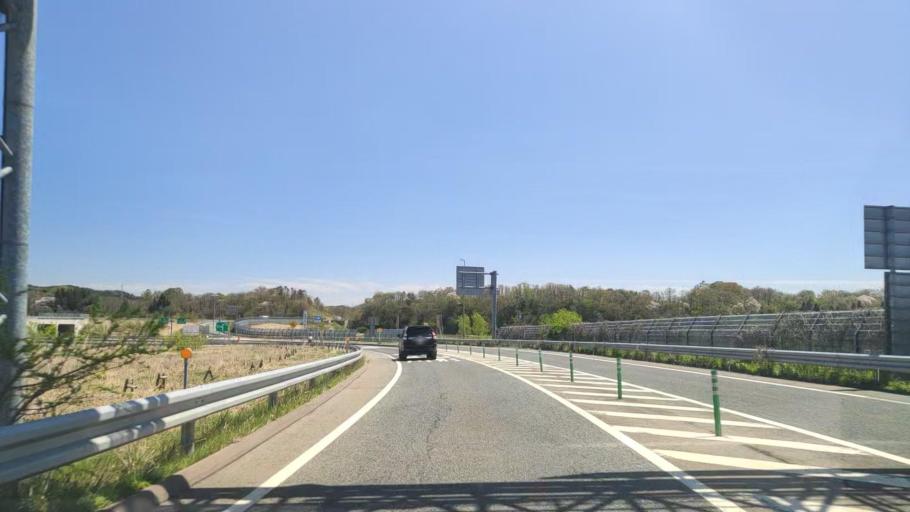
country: JP
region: Yamagata
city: Shinjo
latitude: 38.7404
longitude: 140.2954
